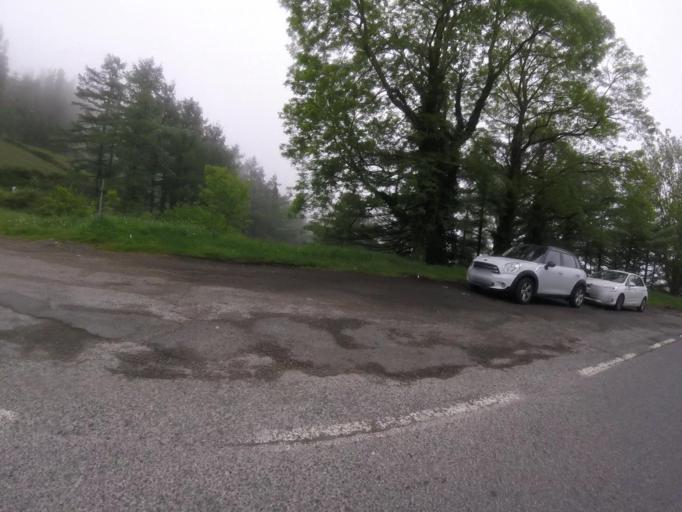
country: ES
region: Navarre
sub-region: Provincia de Navarra
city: Zugarramurdi
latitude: 43.2362
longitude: -1.4942
